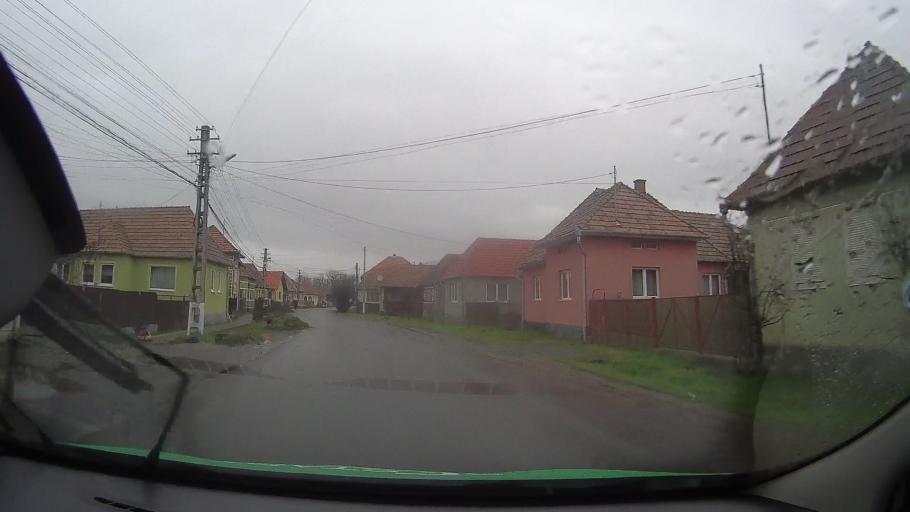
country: RO
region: Mures
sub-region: Comuna Alunis
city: Alunis
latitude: 46.8946
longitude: 24.8207
